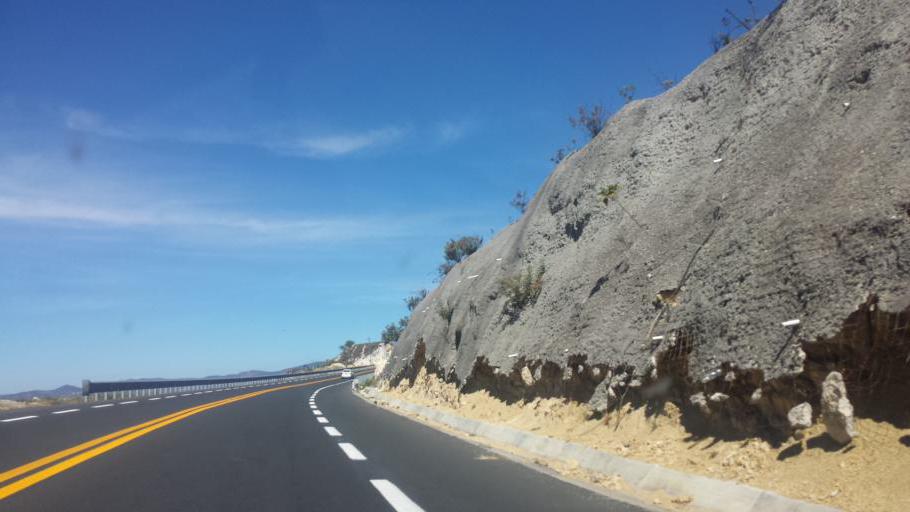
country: MX
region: Puebla
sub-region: San Jose Miahuatlan
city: San Pedro Tetitlan
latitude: 18.0074
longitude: -97.3559
